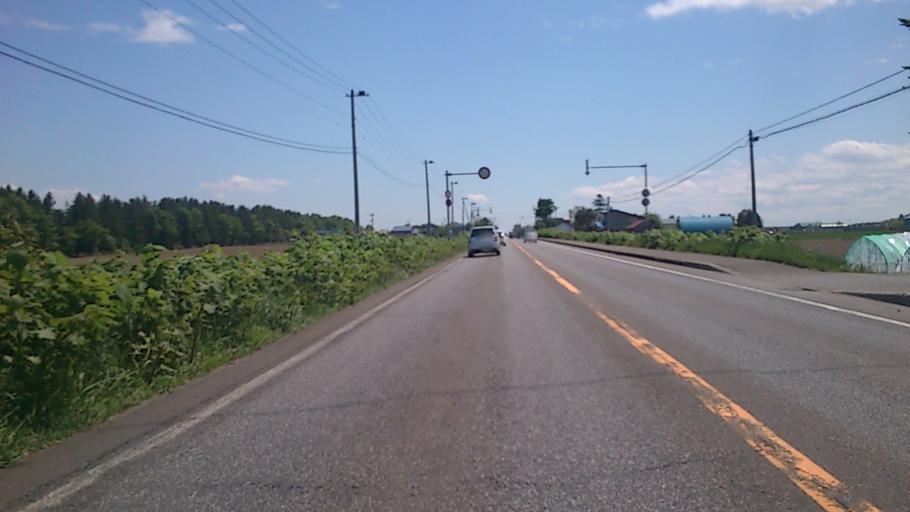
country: JP
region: Hokkaido
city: Nayoro
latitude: 44.2500
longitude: 142.3947
